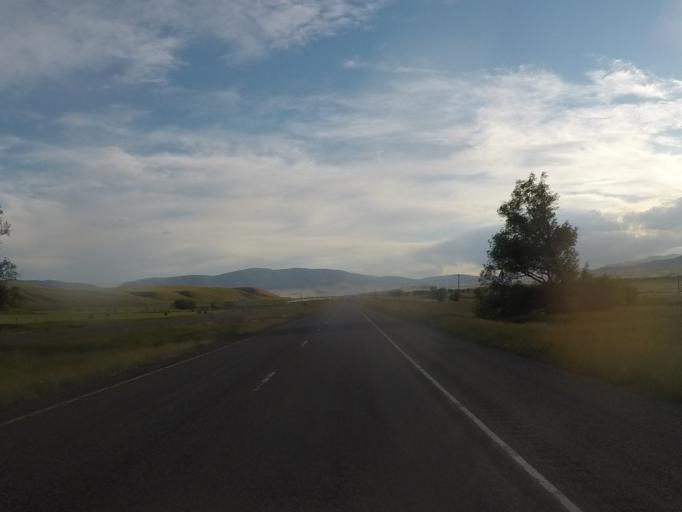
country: US
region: Montana
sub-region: Park County
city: Livingston
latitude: 45.7037
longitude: -110.4630
